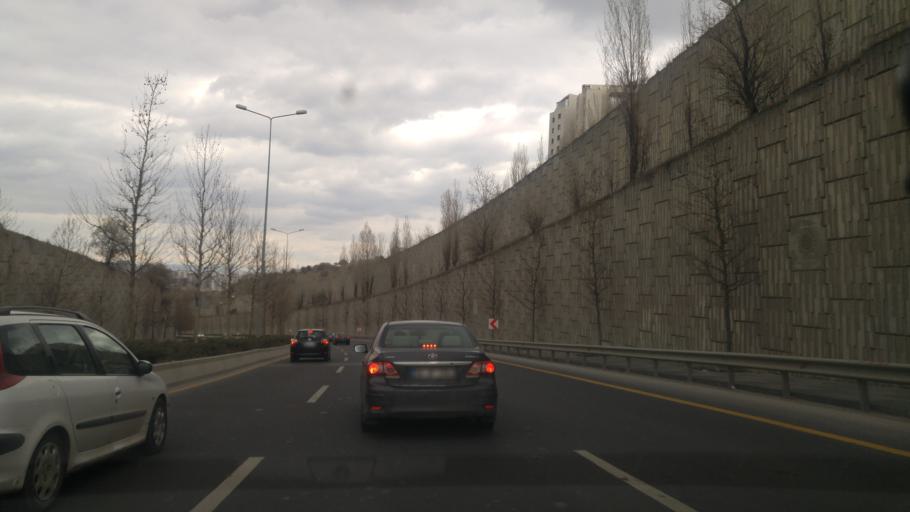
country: TR
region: Ankara
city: Cankaya
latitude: 39.8870
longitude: 32.8937
